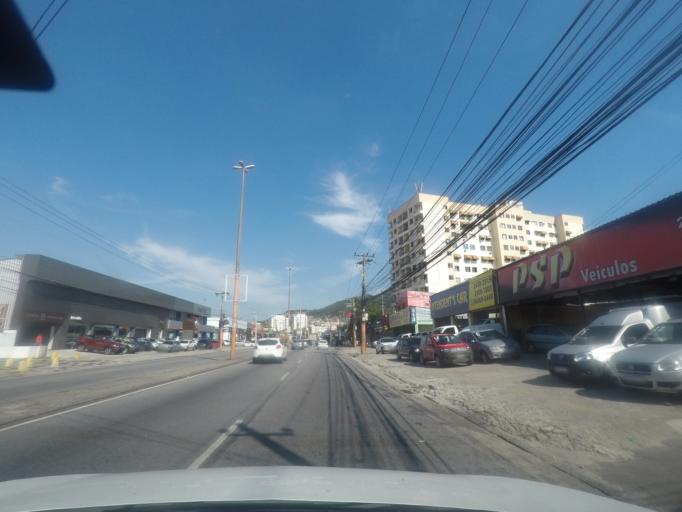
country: BR
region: Rio de Janeiro
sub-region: Sao Joao De Meriti
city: Sao Joao de Meriti
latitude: -22.8817
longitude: -43.3507
